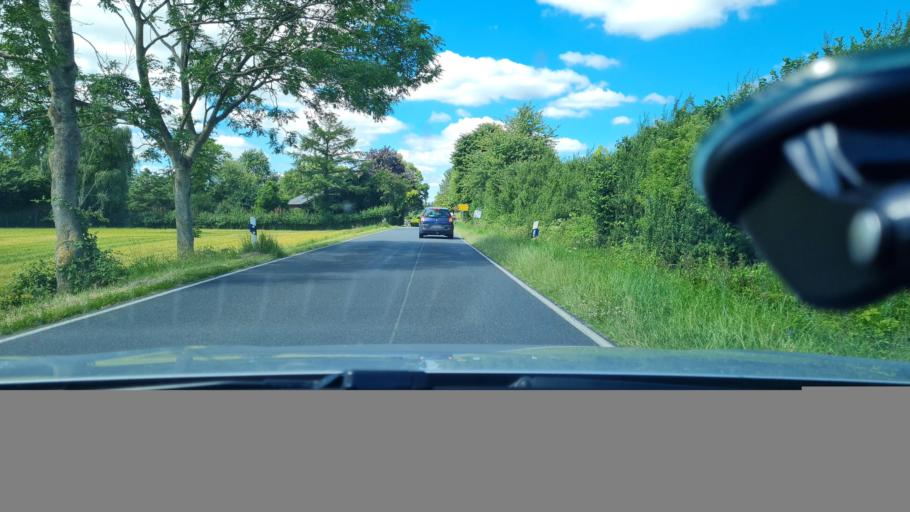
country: DE
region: Schleswig-Holstein
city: Holzdorf
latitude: 54.5908
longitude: 9.8713
